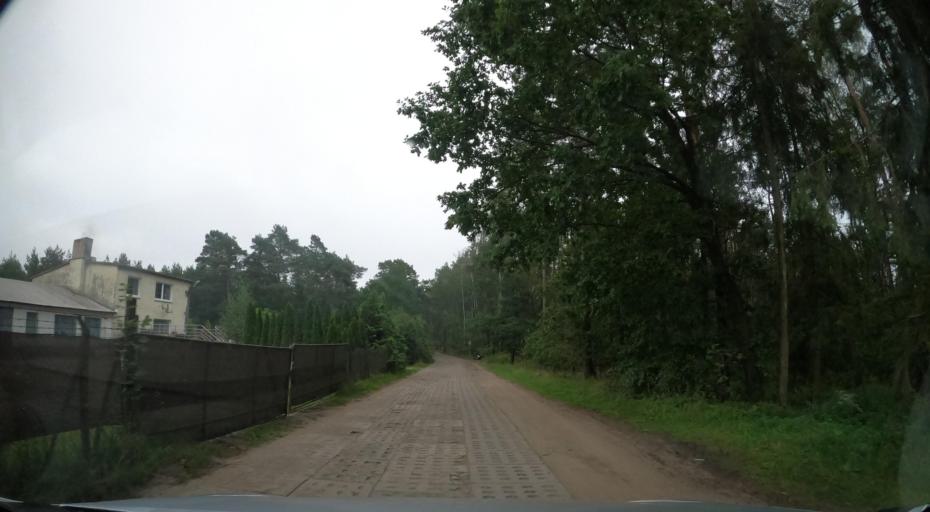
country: PL
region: Pomeranian Voivodeship
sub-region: Powiat kartuski
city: Chwaszczyno
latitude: 54.4205
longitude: 18.4213
